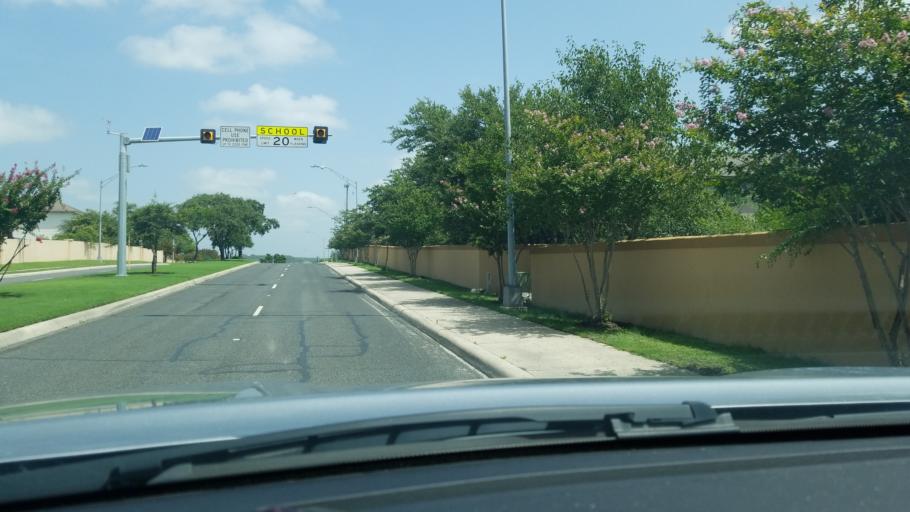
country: US
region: Texas
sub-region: Bexar County
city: Hollywood Park
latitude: 29.6536
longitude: -98.4951
